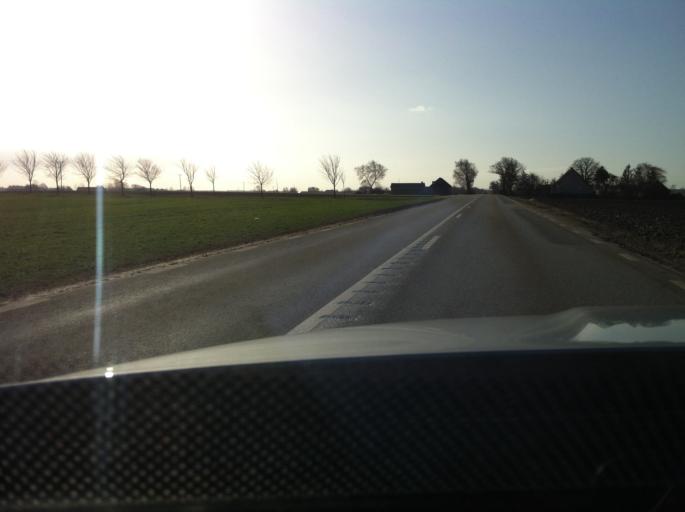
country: SE
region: Skane
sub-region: Landskrona
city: Asmundtorp
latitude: 55.8600
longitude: 12.9750
